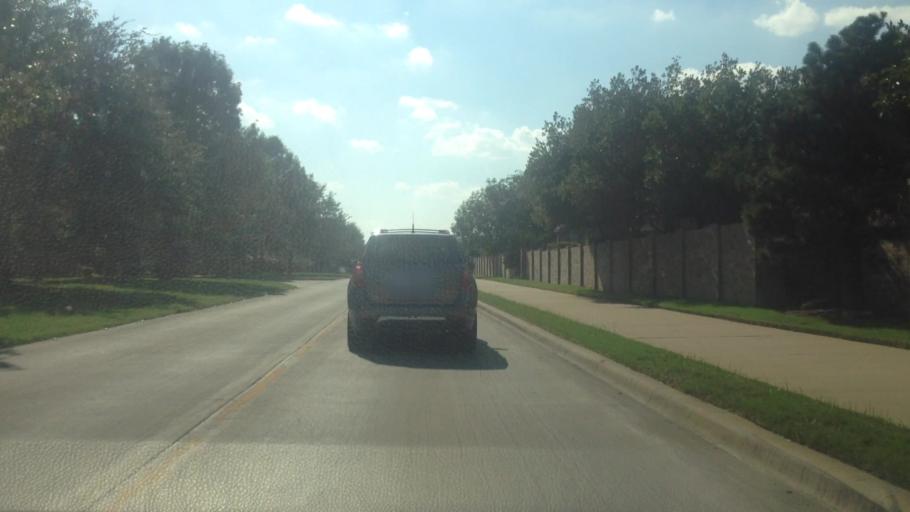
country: US
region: Texas
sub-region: Tarrant County
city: Colleyville
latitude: 32.8805
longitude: -97.1741
